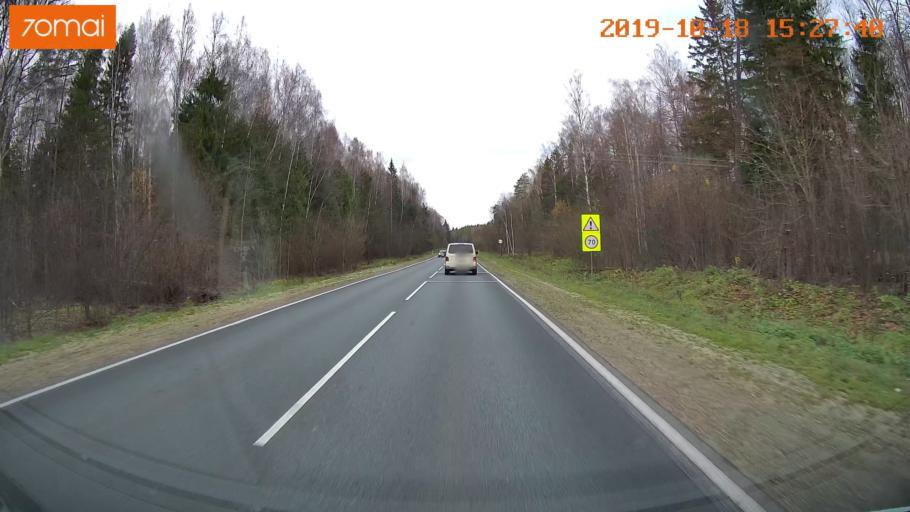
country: RU
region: Vladimir
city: Anopino
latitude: 55.7563
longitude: 40.6718
